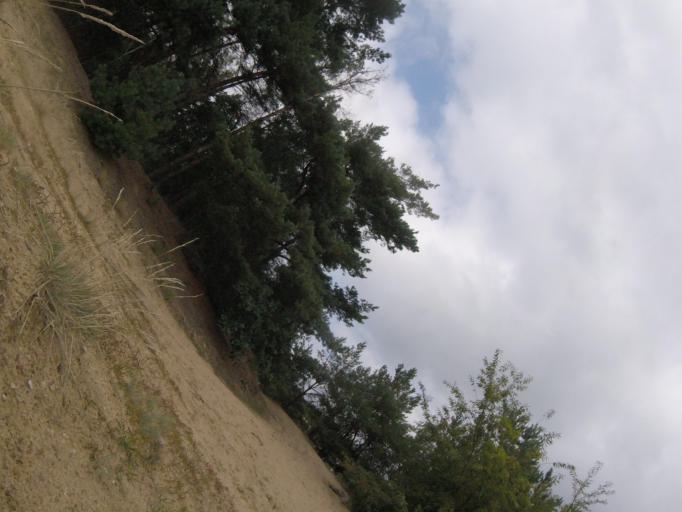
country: DE
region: Brandenburg
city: Gross Koris
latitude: 52.2034
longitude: 13.6560
